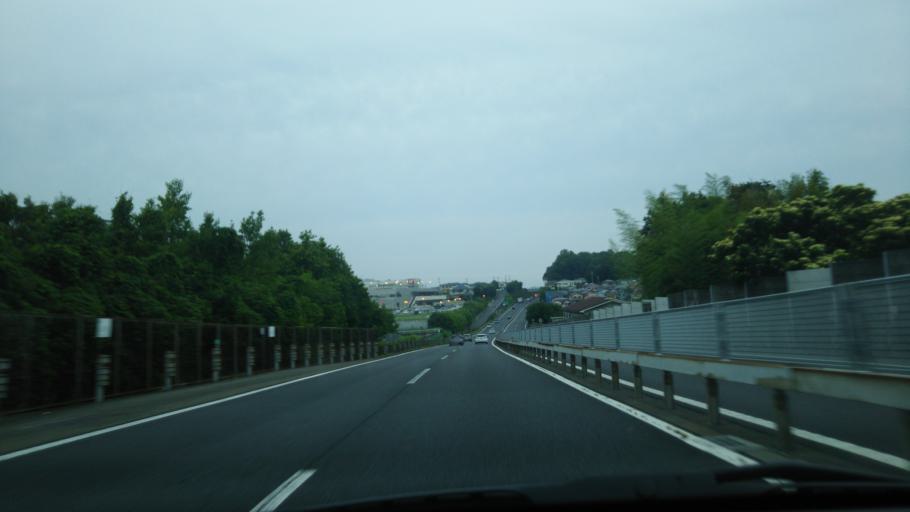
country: JP
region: Kanagawa
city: Oiso
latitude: 35.3458
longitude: 139.2970
